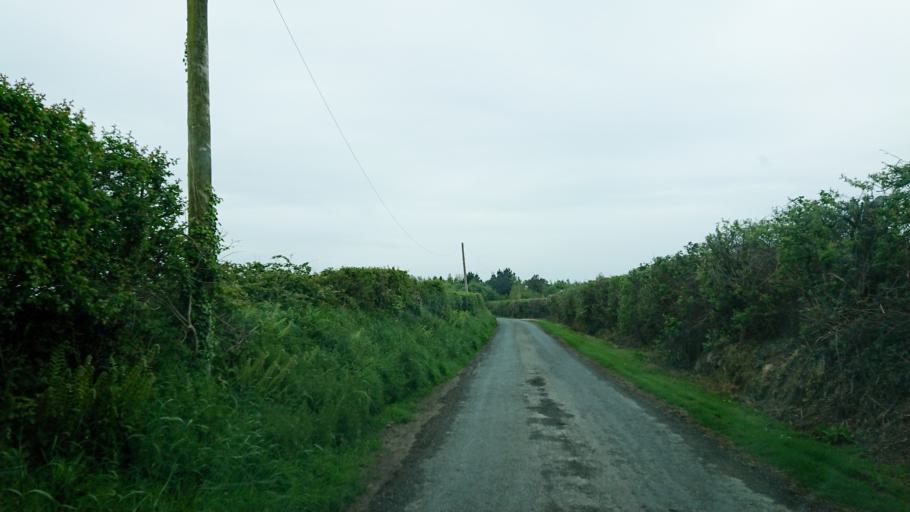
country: IE
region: Munster
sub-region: Waterford
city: Dunmore East
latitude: 52.2248
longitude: -7.0249
